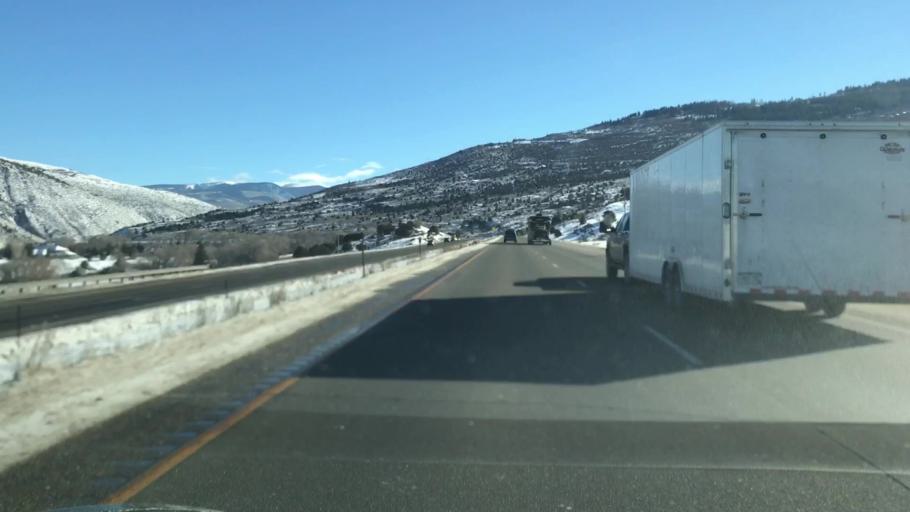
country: US
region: Colorado
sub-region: Eagle County
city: Edwards
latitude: 39.6902
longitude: -106.6623
